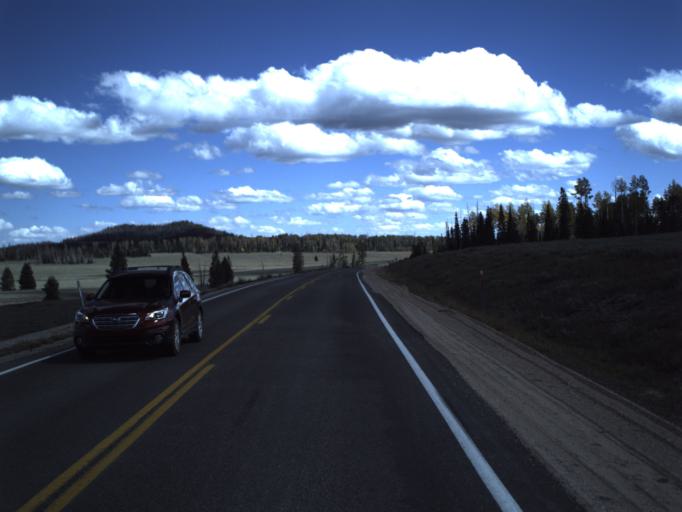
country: US
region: Utah
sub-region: Iron County
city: Parowan
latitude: 37.5698
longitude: -112.7979
